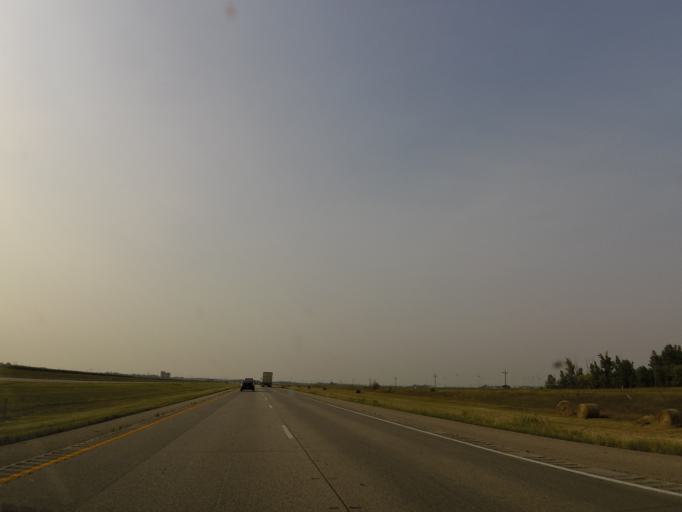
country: US
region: Minnesota
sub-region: Clay County
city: Oakport
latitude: 46.9497
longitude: -96.8597
